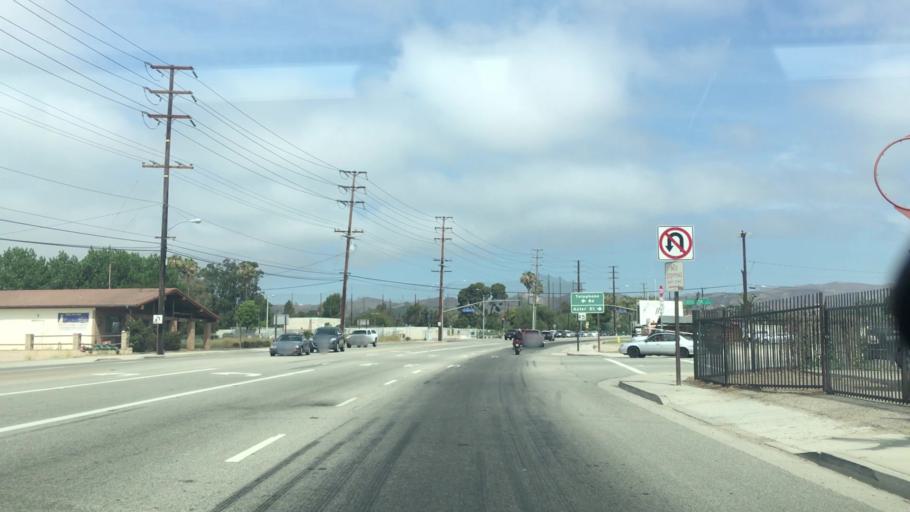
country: US
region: California
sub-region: Ventura County
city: Saticoy
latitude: 34.2828
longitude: -119.1498
